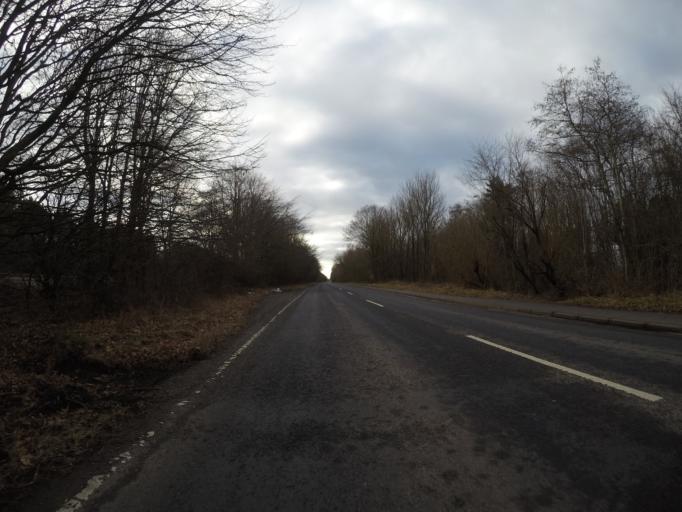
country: GB
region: Scotland
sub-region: North Ayrshire
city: Dreghorn
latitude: 55.5824
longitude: -4.6451
